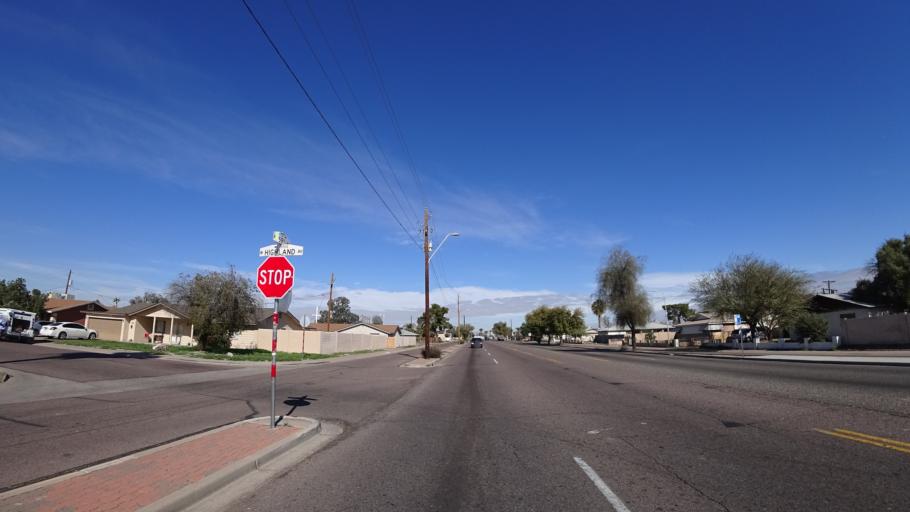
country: US
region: Arizona
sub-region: Maricopa County
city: Glendale
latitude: 33.5062
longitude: -112.1865
